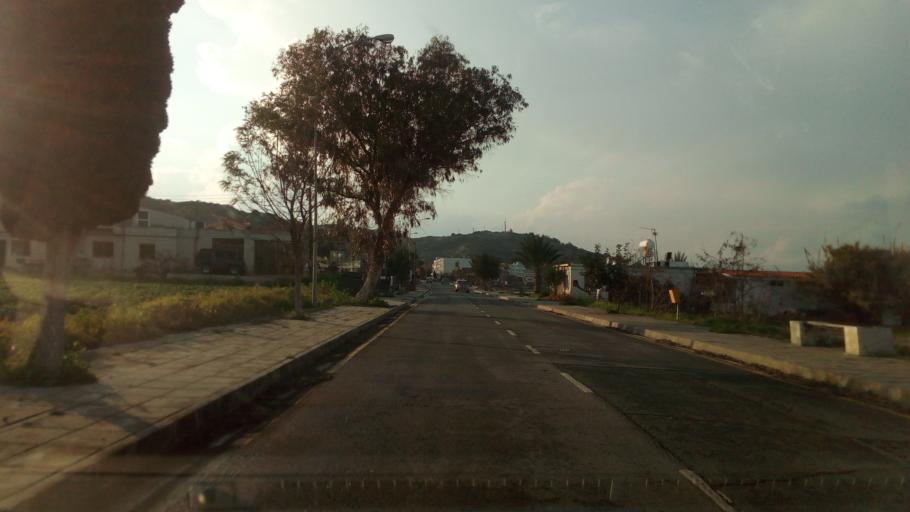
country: CY
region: Lefkosia
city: Kato Pyrgos
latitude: 35.1870
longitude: 32.6756
